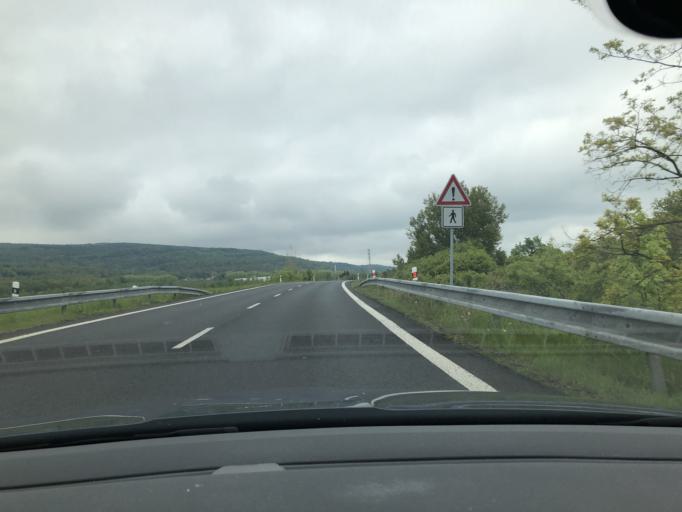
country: CZ
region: Ustecky
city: Libouchec
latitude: 50.7193
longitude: 14.0071
